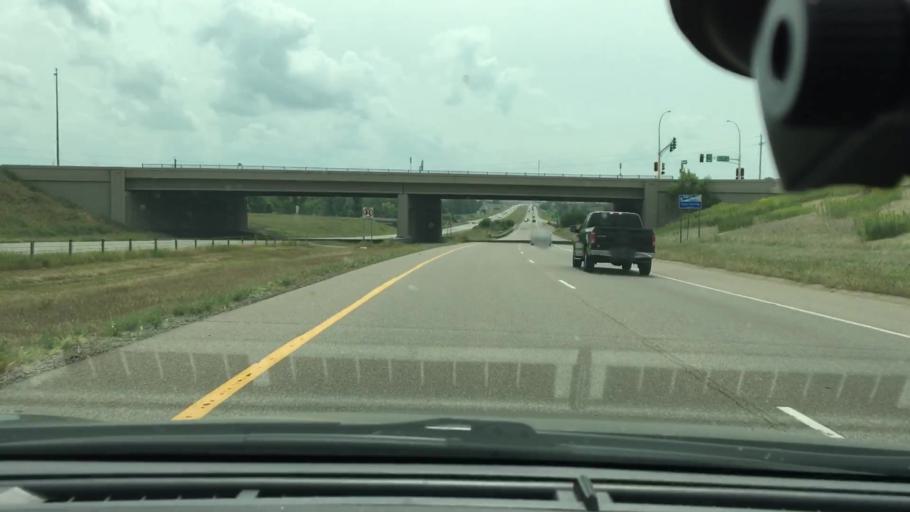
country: US
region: Minnesota
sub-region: Hennepin County
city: Dayton
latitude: 45.2303
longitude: -93.5526
